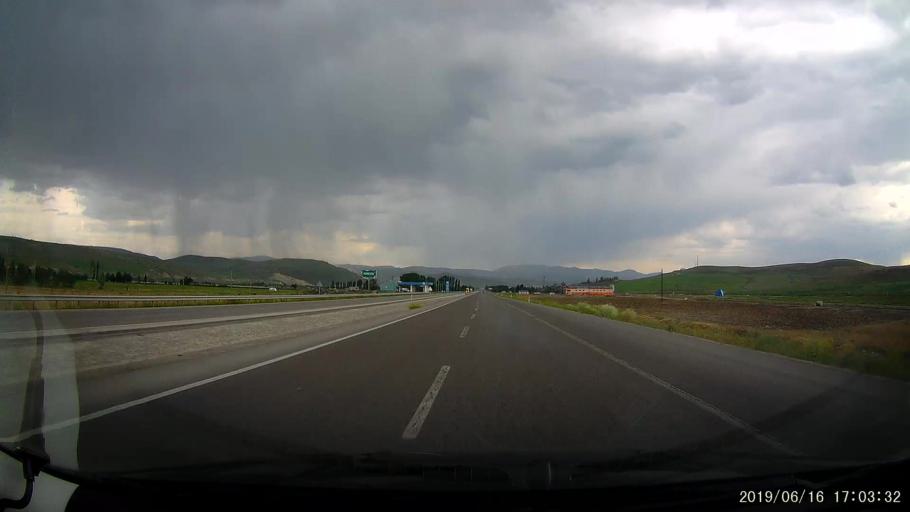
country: TR
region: Erzurum
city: Askale
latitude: 39.9358
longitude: 40.7294
